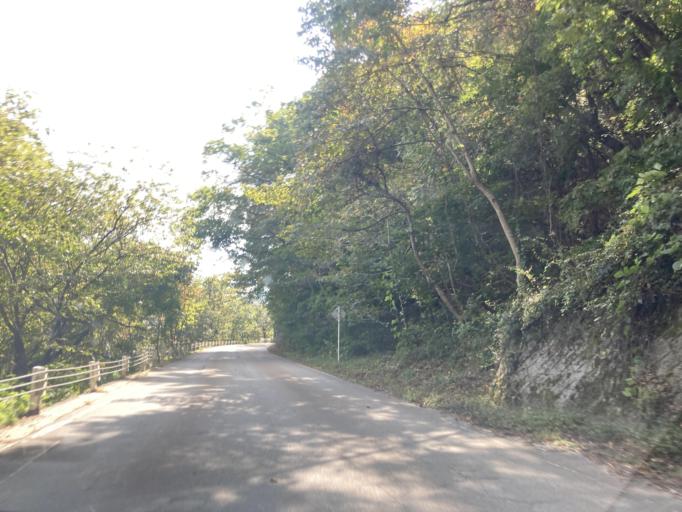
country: JP
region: Nagano
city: Omachi
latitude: 36.5255
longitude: 137.7901
